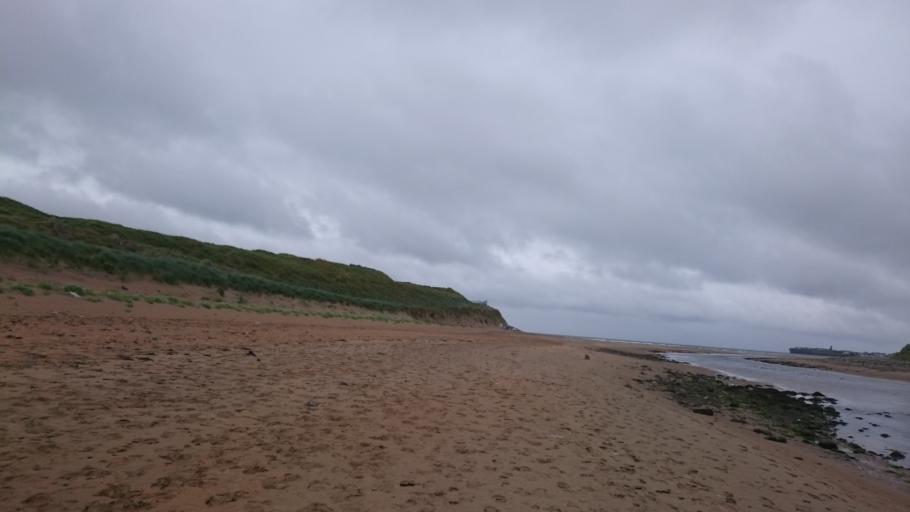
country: IE
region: Munster
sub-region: An Clar
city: Kilrush
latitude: 52.9443
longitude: -9.3557
